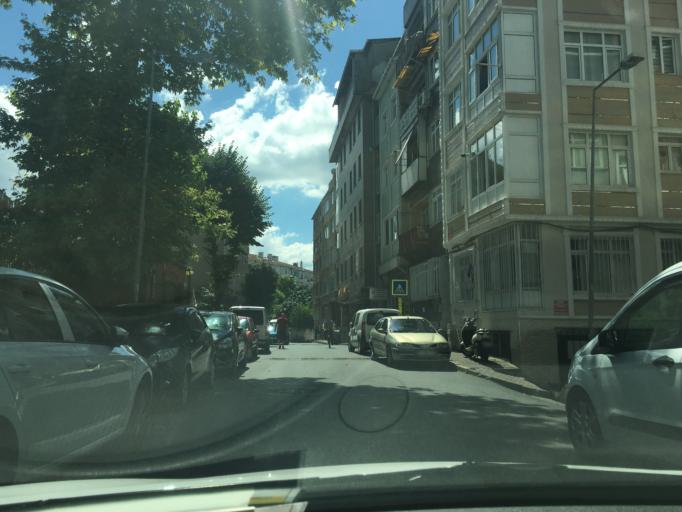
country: TR
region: Istanbul
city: Istanbul
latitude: 41.0094
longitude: 28.9283
